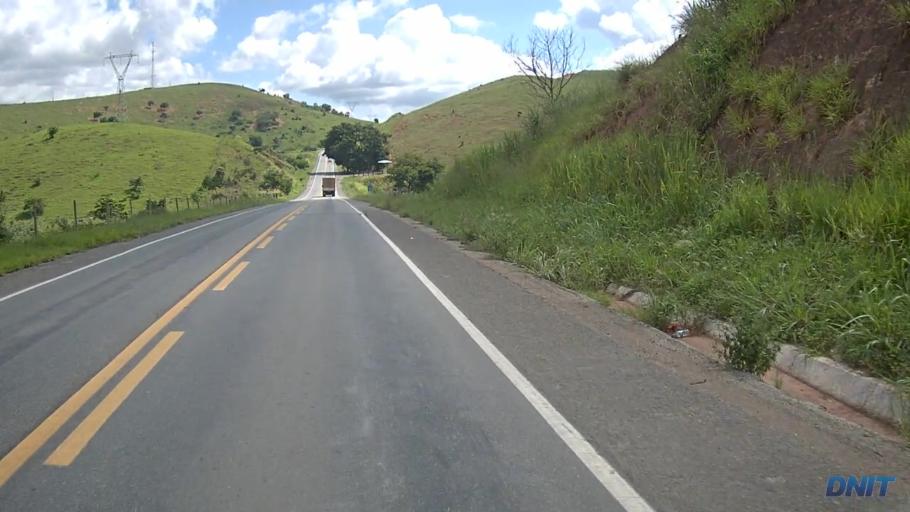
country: BR
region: Minas Gerais
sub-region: Governador Valadares
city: Governador Valadares
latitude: -19.0294
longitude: -42.1479
